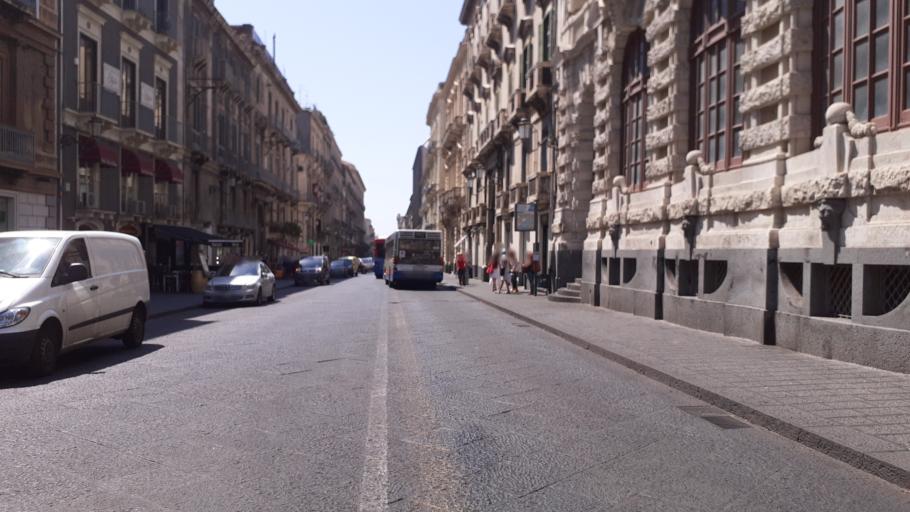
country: IT
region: Sicily
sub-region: Catania
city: Catania
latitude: 37.5102
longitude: 15.0856
